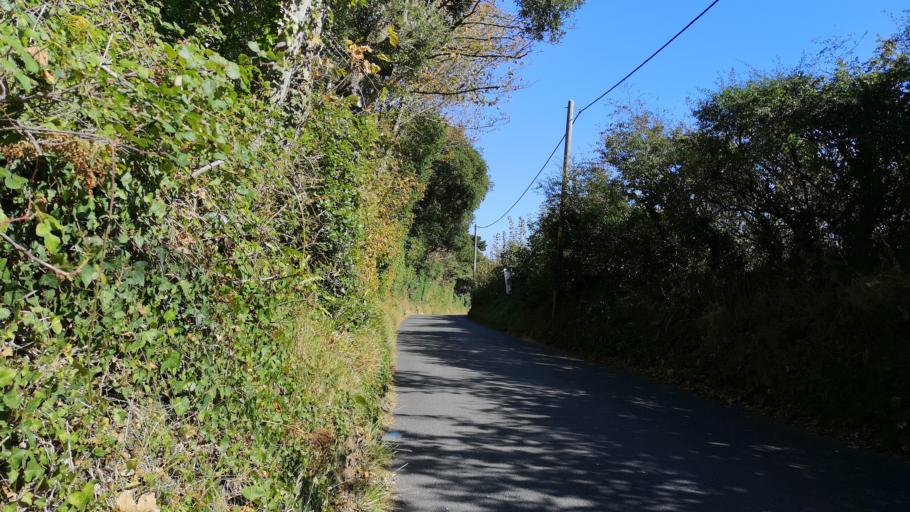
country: GB
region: England
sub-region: Isle of Wight
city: Totland
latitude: 50.6726
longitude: -1.5394
